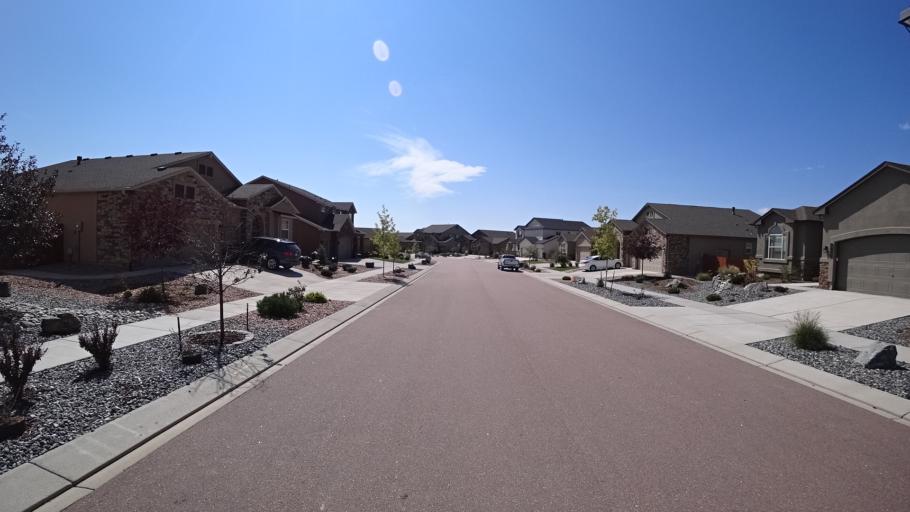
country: US
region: Colorado
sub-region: El Paso County
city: Cimarron Hills
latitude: 38.9335
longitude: -104.6847
